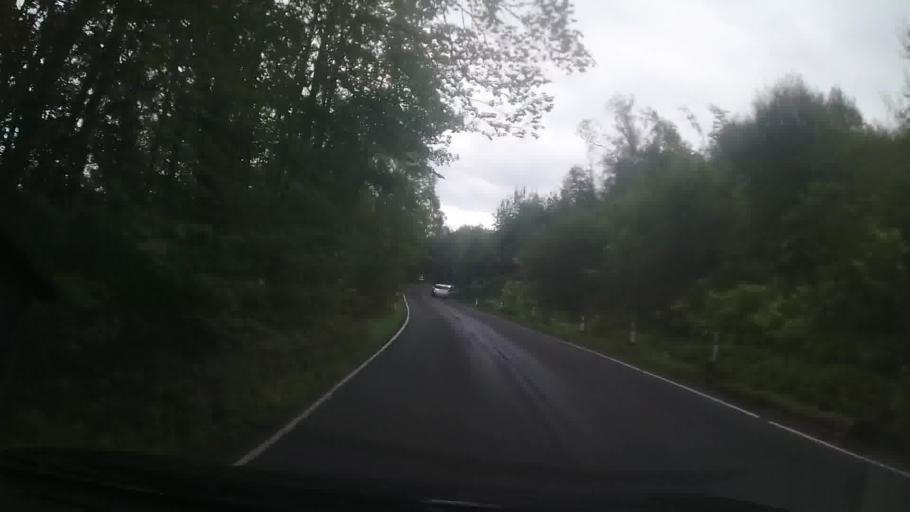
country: GB
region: Scotland
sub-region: Argyll and Bute
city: Garelochhead
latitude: 56.2377
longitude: -5.0797
